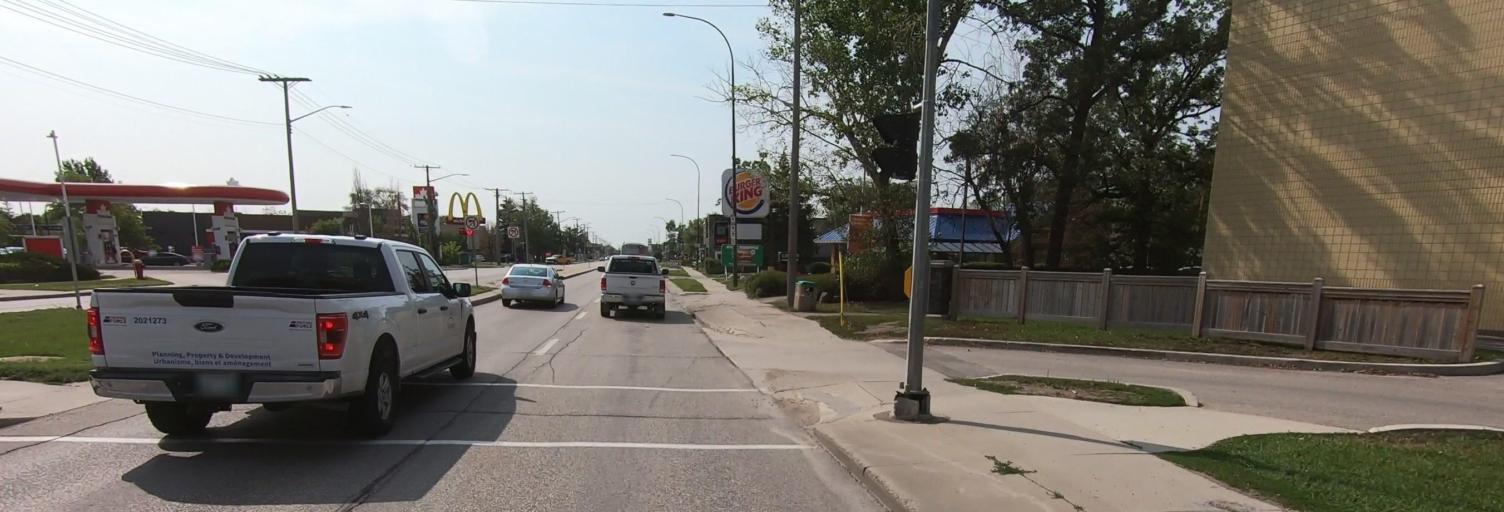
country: CA
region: Manitoba
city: Winnipeg
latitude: 49.8277
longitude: -97.1147
